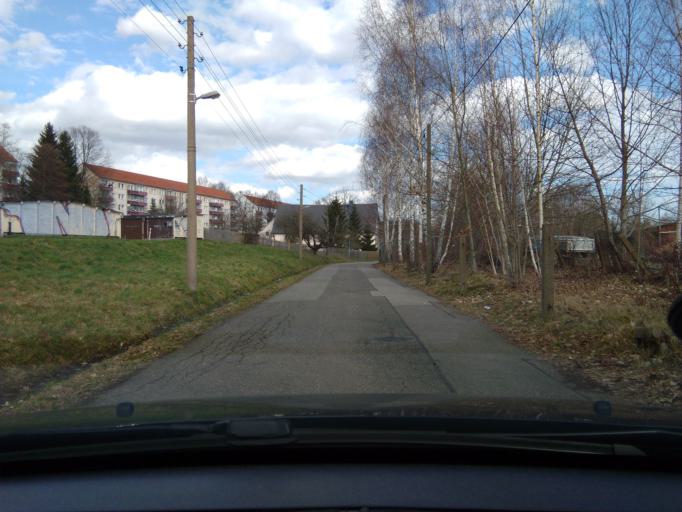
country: DE
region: Saxony
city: Chemnitz
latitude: 50.8362
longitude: 12.8837
